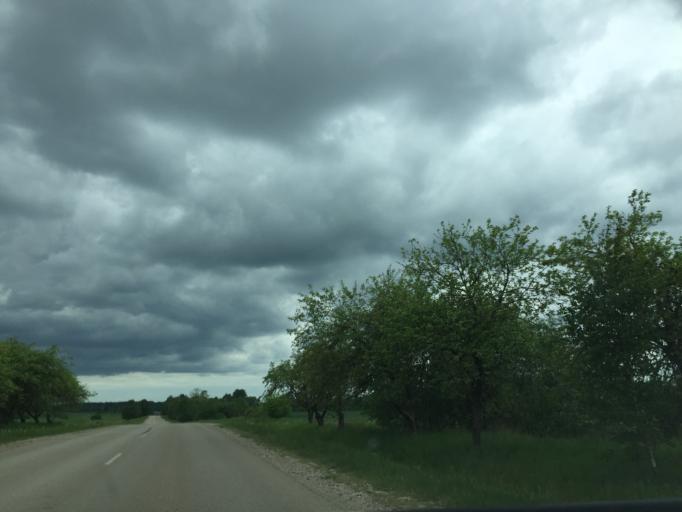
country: LV
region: Dagda
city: Dagda
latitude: 56.1006
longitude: 27.5128
